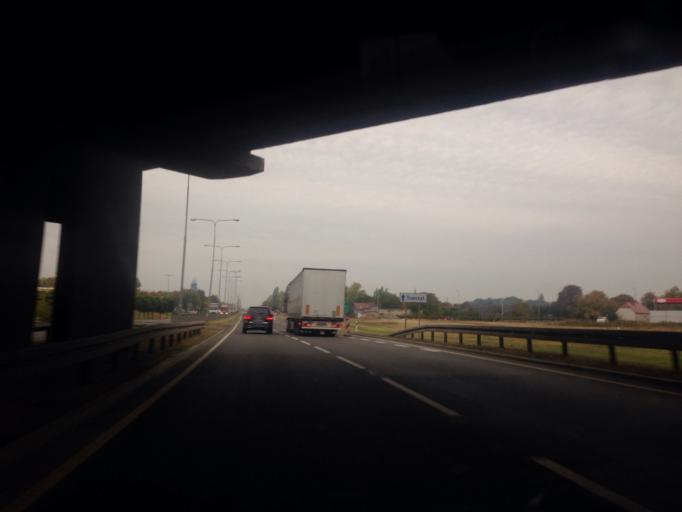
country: PL
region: Greater Poland Voivodeship
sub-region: Powiat gnieznienski
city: Gniezno
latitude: 52.5456
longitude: 17.6042
